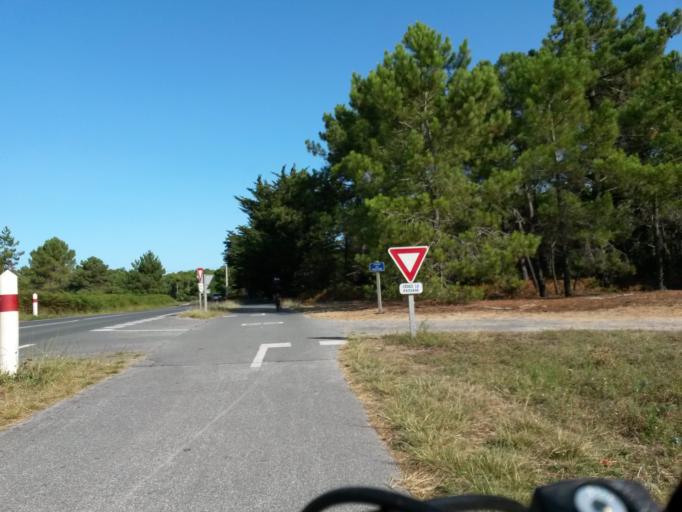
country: FR
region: Poitou-Charentes
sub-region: Departement de la Charente-Maritime
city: Saint-Martin-de-Re
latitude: 46.1701
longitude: -1.3626
